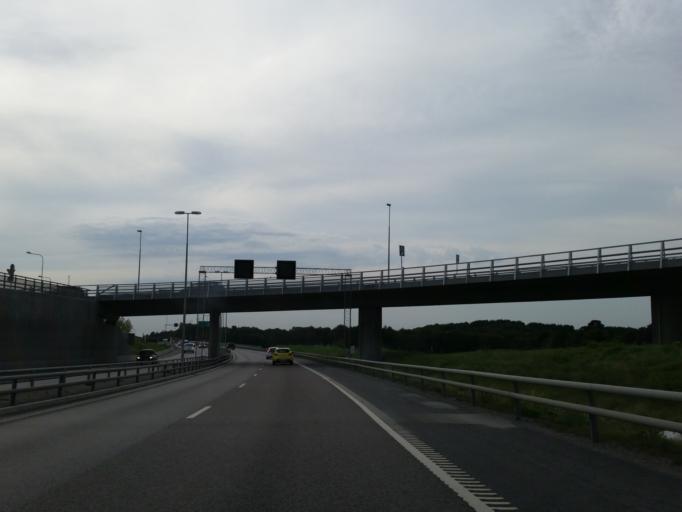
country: SE
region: Stockholm
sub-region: Stockholms Kommun
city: Kista
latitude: 59.3974
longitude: 17.9114
